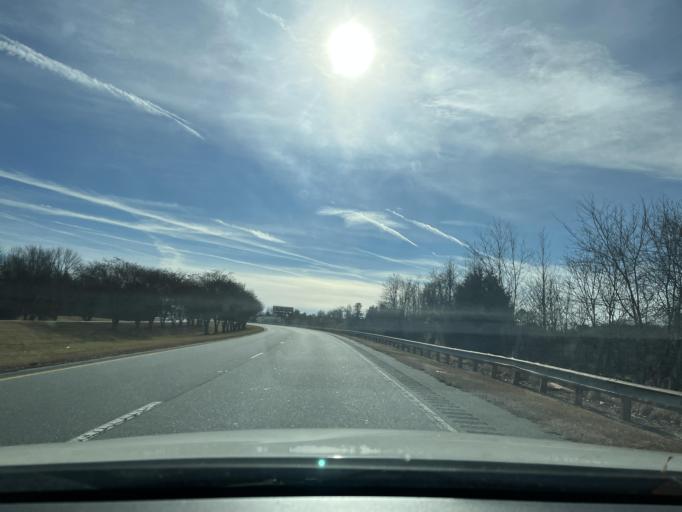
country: US
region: North Carolina
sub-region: Guilford County
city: Greensboro
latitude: 36.0317
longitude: -79.7723
